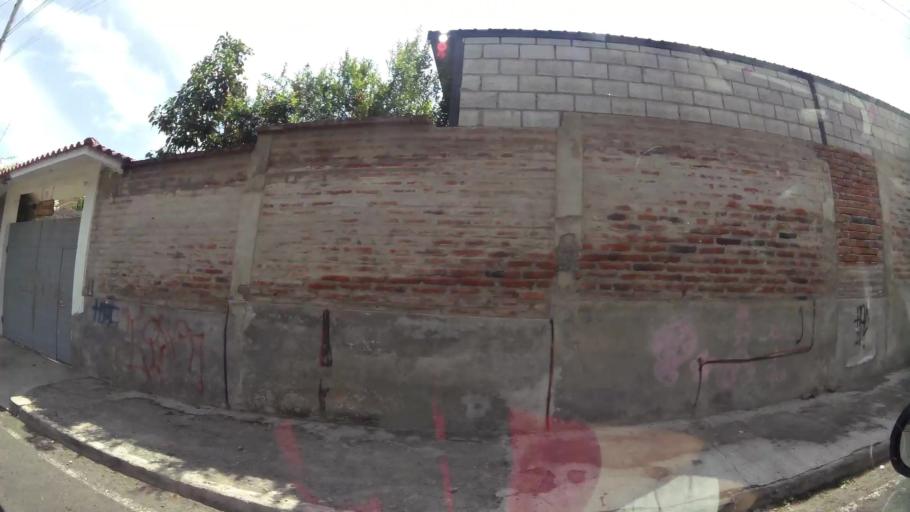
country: EC
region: Pichincha
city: Quito
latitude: -0.2138
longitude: -78.3937
